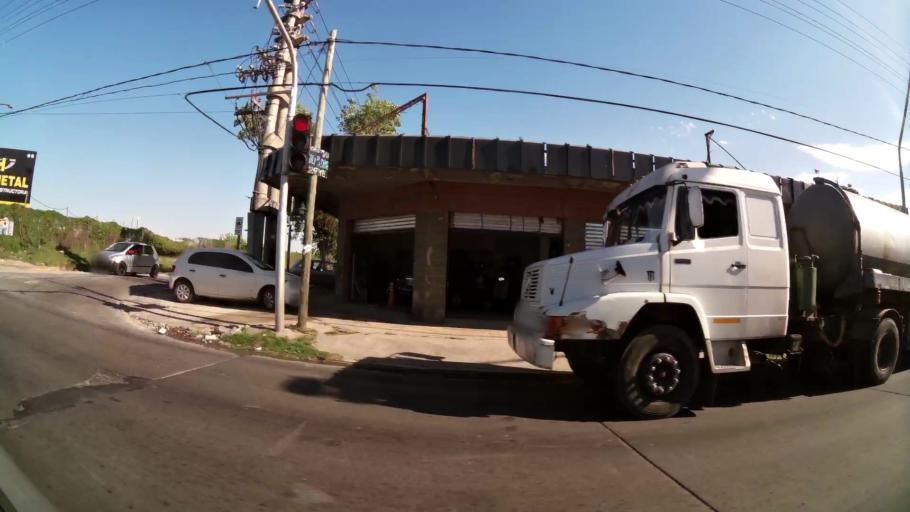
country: AR
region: Buenos Aires
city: Santa Catalina - Dique Lujan
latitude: -34.4781
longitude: -58.6693
